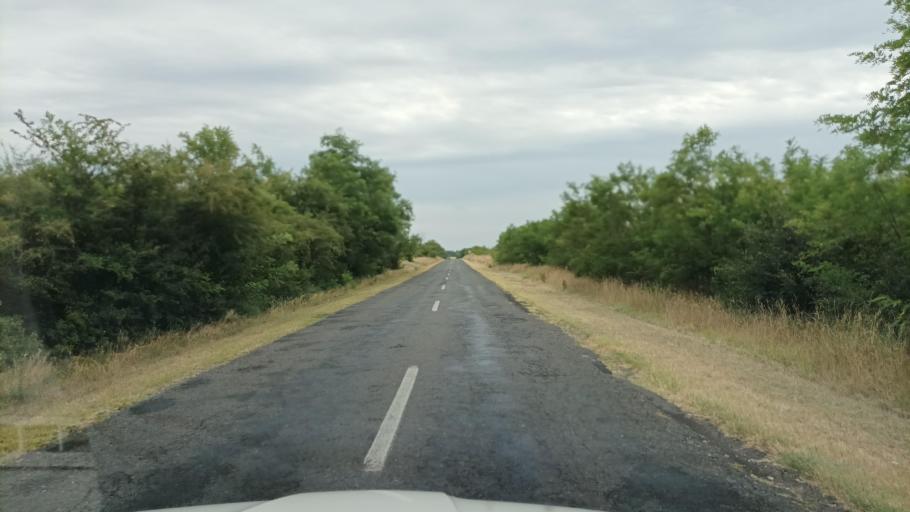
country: HU
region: Pest
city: Dabas
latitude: 47.1308
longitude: 19.3401
